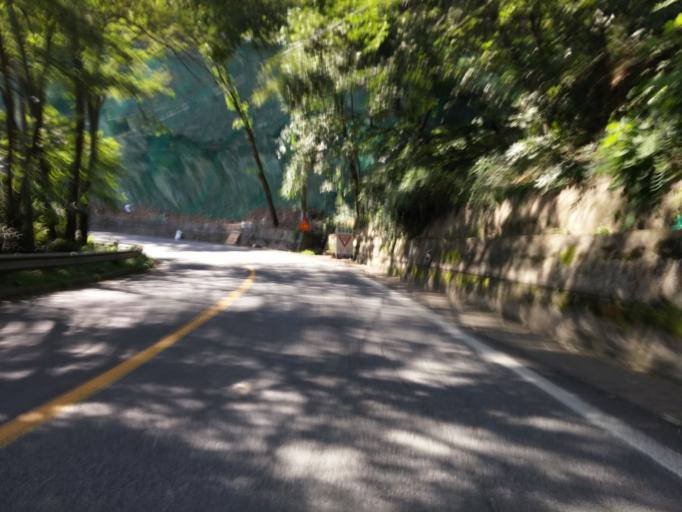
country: KR
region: Daejeon
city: Sintansin
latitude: 36.4787
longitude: 127.4768
